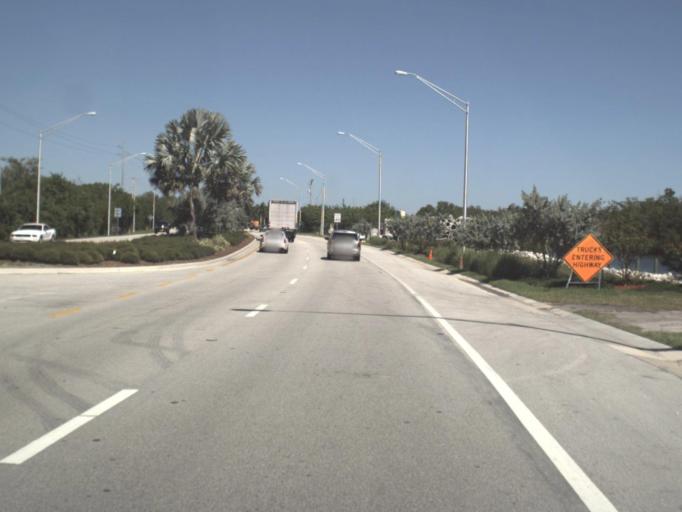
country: US
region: Florida
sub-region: Collier County
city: Marco
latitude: 25.9667
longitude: -81.7082
